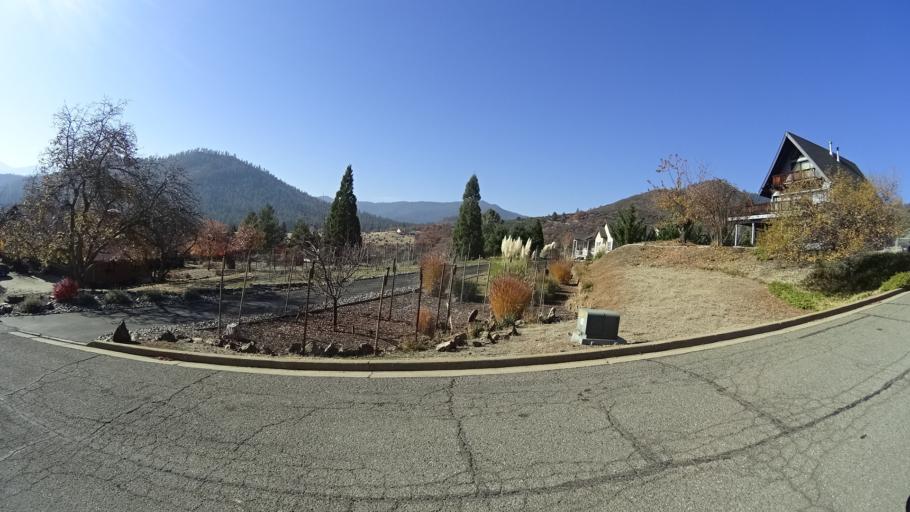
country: US
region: California
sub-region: Siskiyou County
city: Yreka
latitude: 41.7401
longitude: -122.6593
